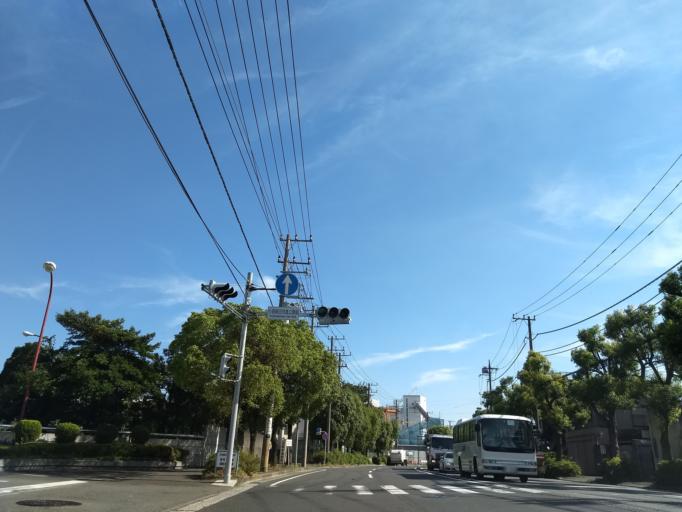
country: JP
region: Kanagawa
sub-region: Kawasaki-shi
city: Kawasaki
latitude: 35.5344
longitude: 139.7510
